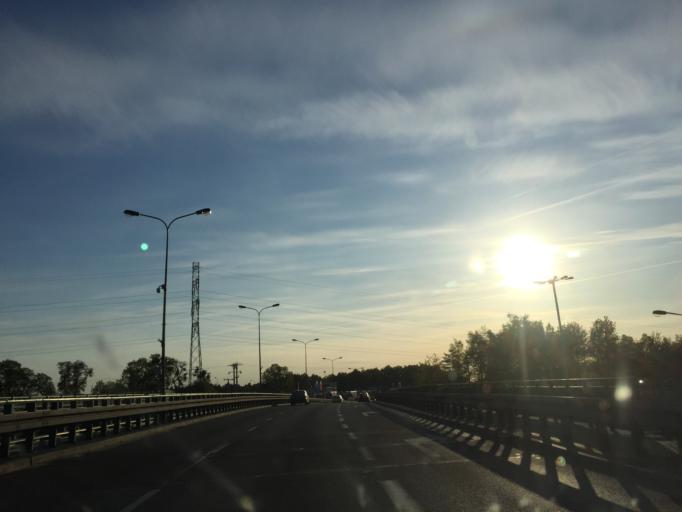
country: PL
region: Pomeranian Voivodeship
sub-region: Sopot
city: Sopot
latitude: 54.3762
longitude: 18.5148
